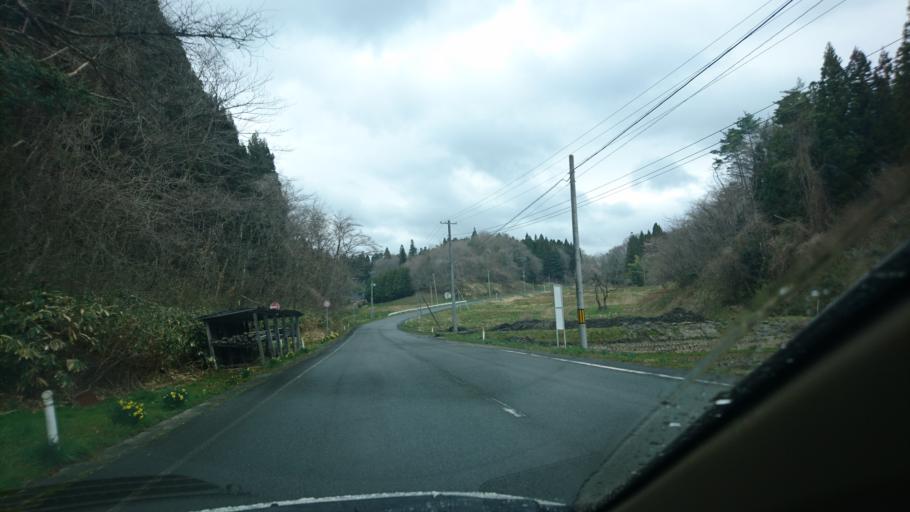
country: JP
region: Iwate
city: Ichinoseki
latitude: 38.9468
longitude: 141.3201
